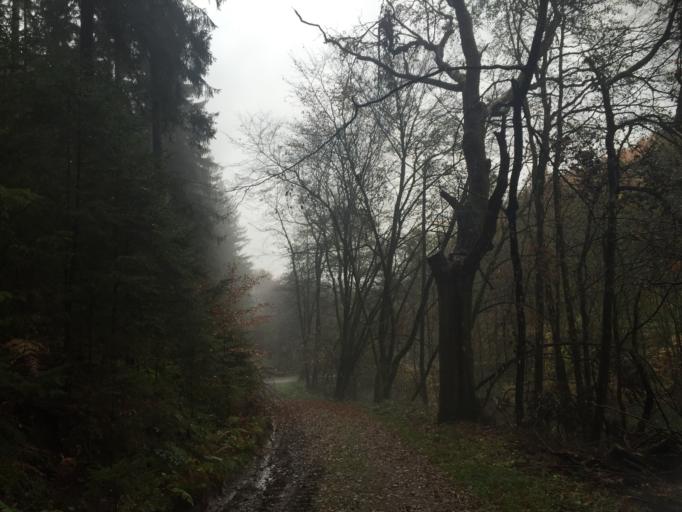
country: DE
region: Hesse
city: Hirschhorn
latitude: 49.4567
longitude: 8.8730
